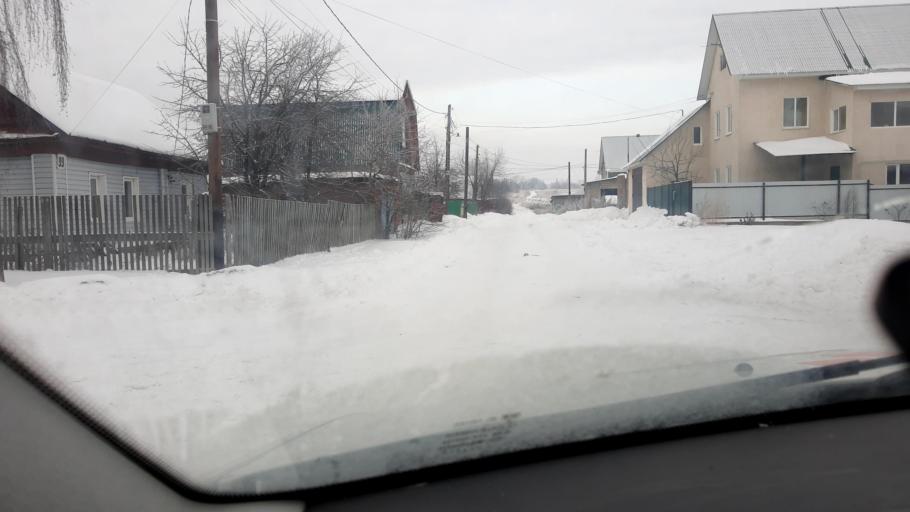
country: RU
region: Bashkortostan
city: Ufa
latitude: 54.8436
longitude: 56.1591
